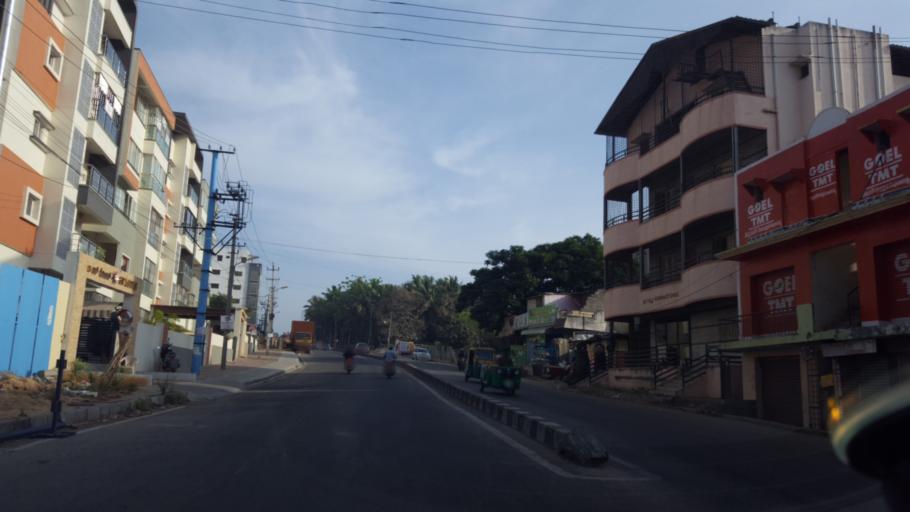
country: IN
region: Karnataka
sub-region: Bangalore Urban
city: Bangalore
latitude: 12.9096
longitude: 77.5134
